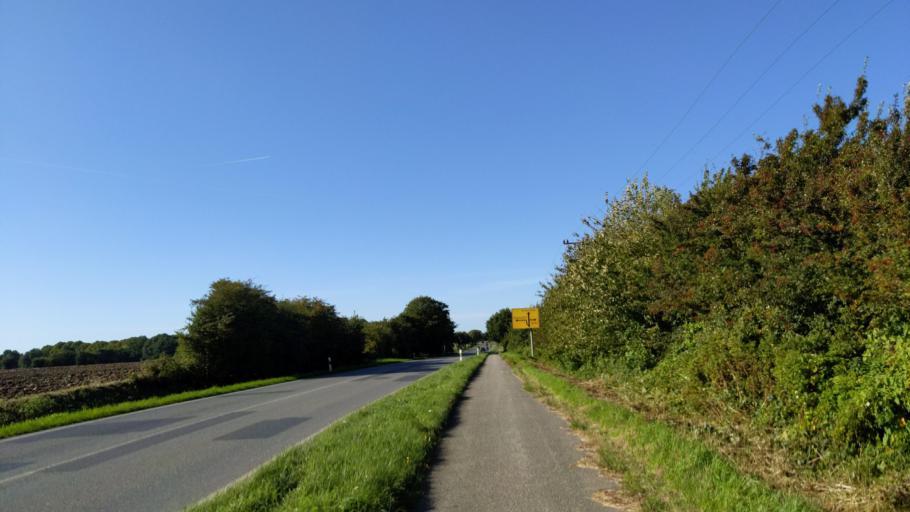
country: DE
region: Schleswig-Holstein
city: Ahrensbok
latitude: 53.9605
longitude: 10.6101
